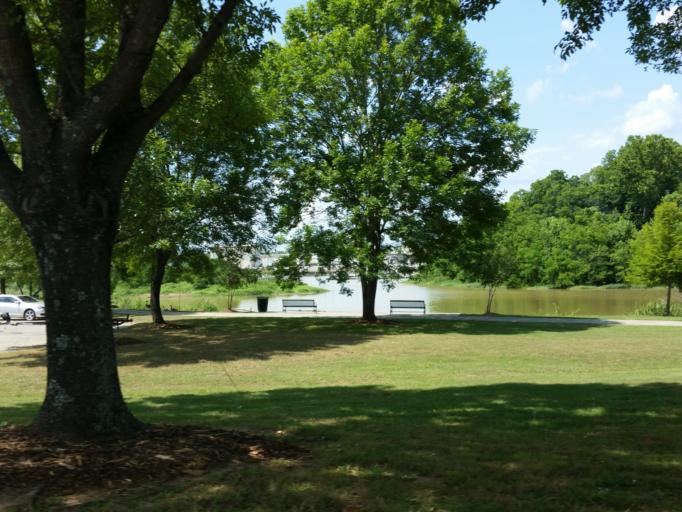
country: US
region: Alabama
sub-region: Marengo County
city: Demopolis
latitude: 32.5246
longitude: -87.8387
